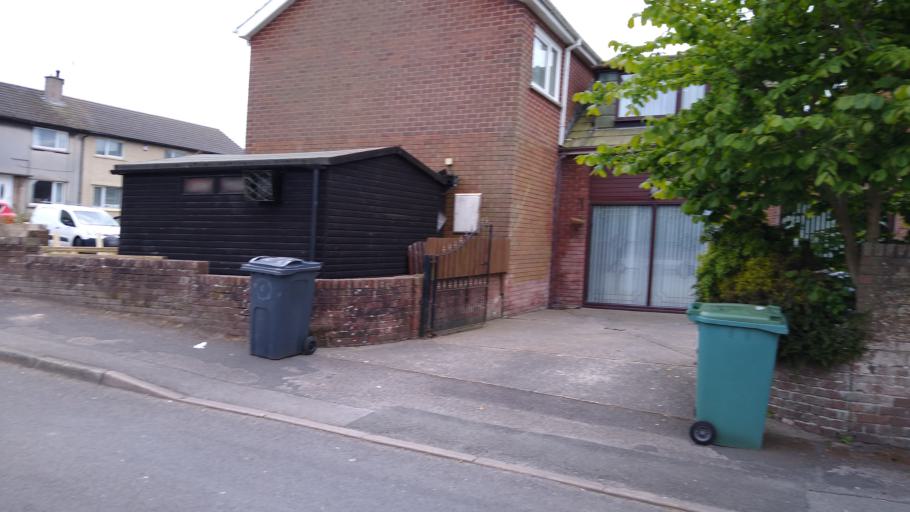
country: GB
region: England
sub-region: Cumbria
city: Dearham
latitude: 54.7310
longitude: -3.4434
